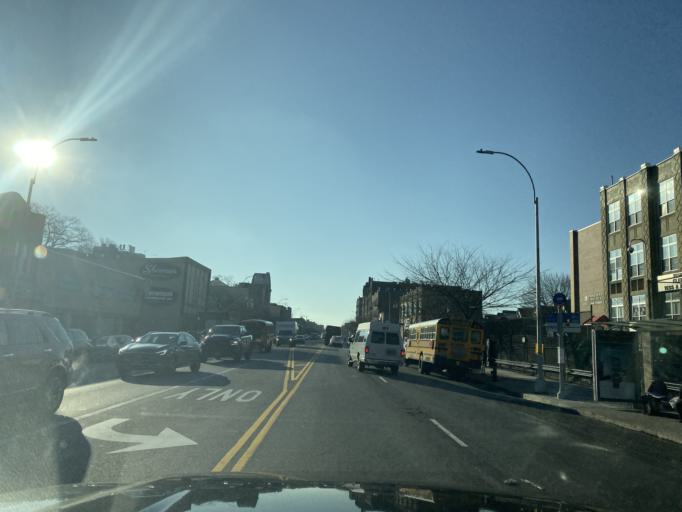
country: US
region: New York
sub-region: Kings County
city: Brooklyn
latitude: 40.6269
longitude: -73.9656
